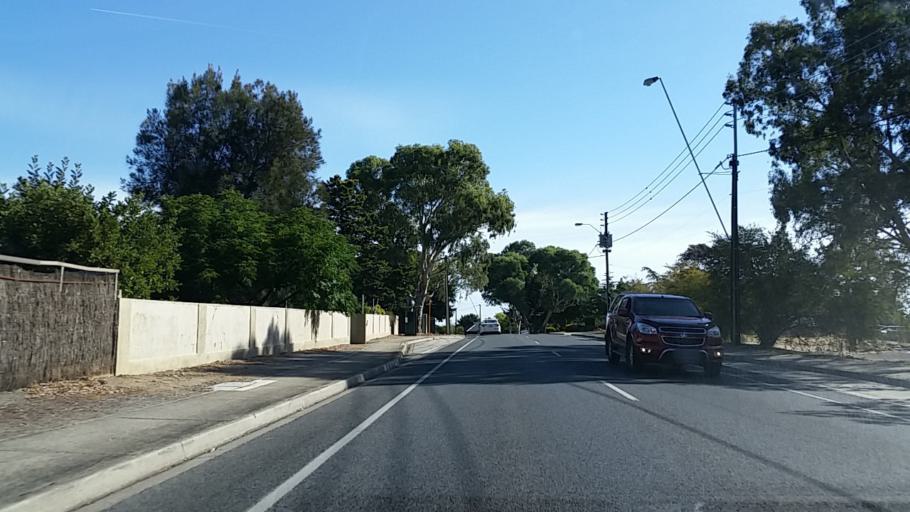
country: AU
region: South Australia
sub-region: Tea Tree Gully
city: Hope Valley
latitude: -34.8429
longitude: 138.7197
